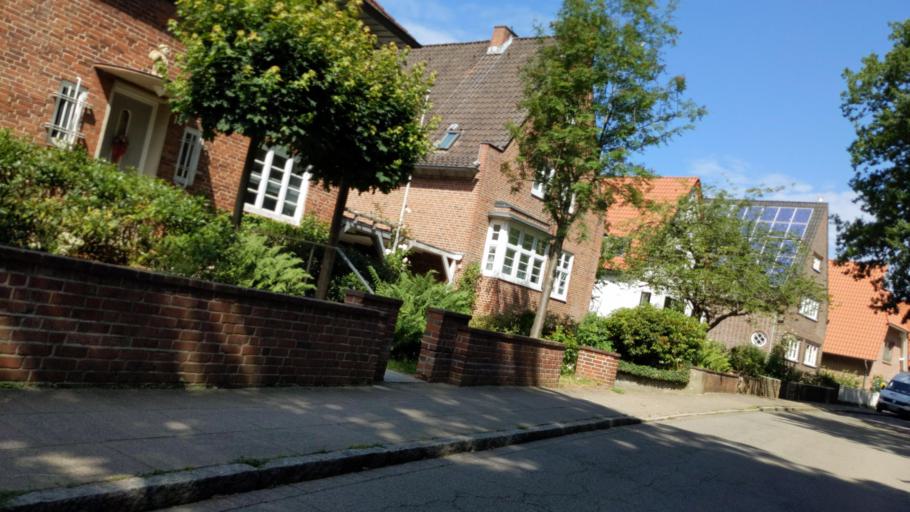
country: DE
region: Schleswig-Holstein
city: Ploen
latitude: 54.1563
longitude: 10.4314
